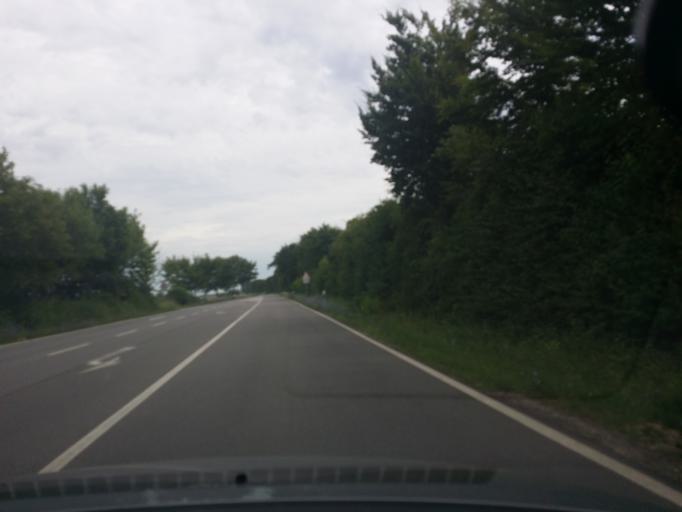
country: DE
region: Rheinland-Pfalz
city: Spiesheim
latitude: 49.7932
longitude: 8.1414
